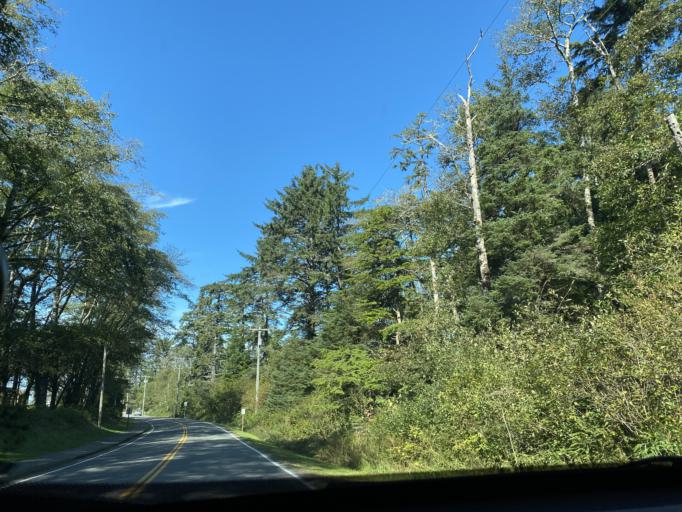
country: US
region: Washington
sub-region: Clallam County
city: Forks
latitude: 47.9049
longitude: -124.6302
